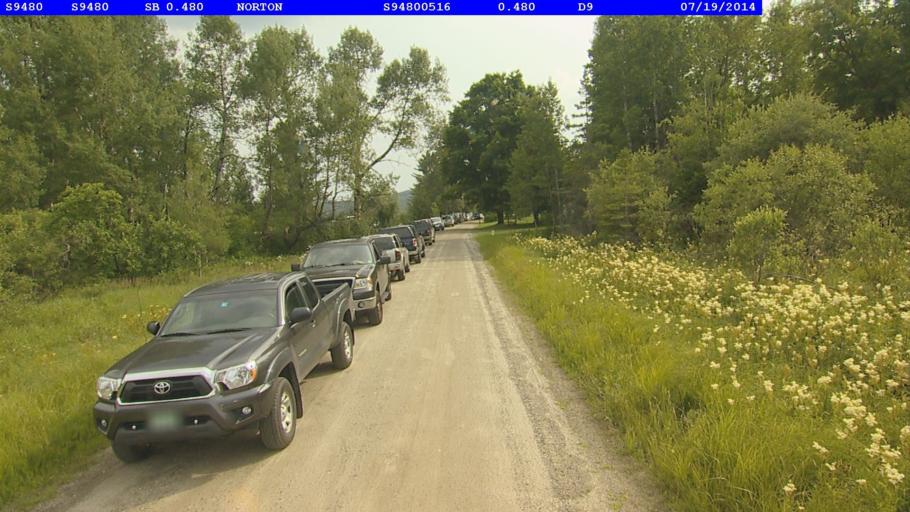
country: CA
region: Quebec
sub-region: Estrie
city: Coaticook
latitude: 44.9974
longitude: -71.7103
